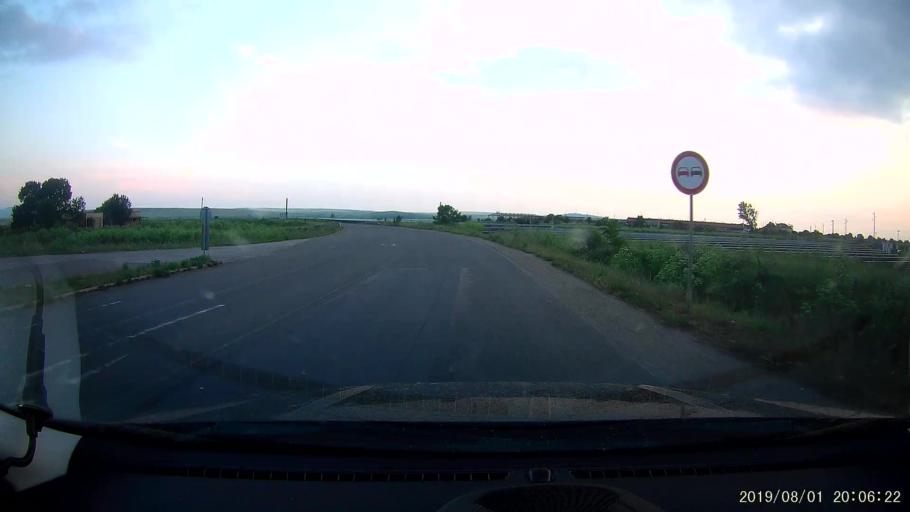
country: BG
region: Yambol
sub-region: Obshtina Yambol
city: Yambol
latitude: 42.5357
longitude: 26.5564
